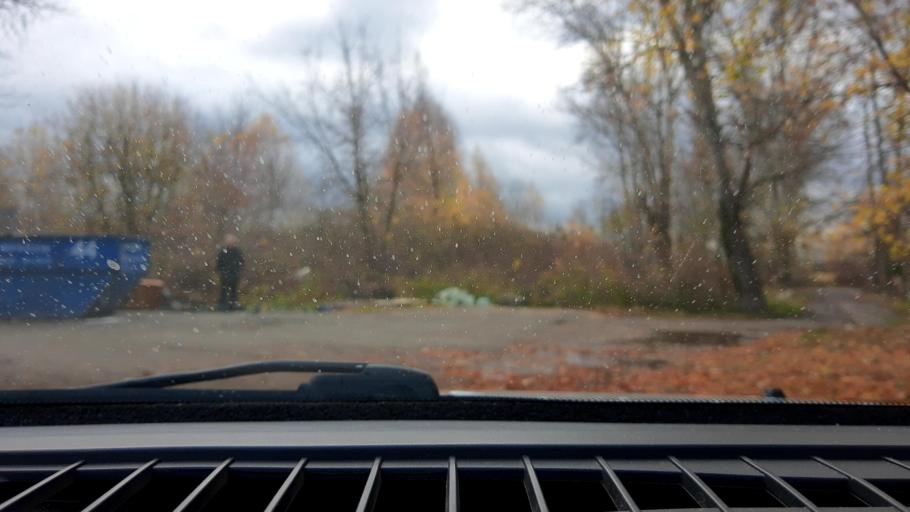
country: RU
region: Nizjnij Novgorod
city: Nizhniy Novgorod
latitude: 56.3013
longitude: 43.8846
